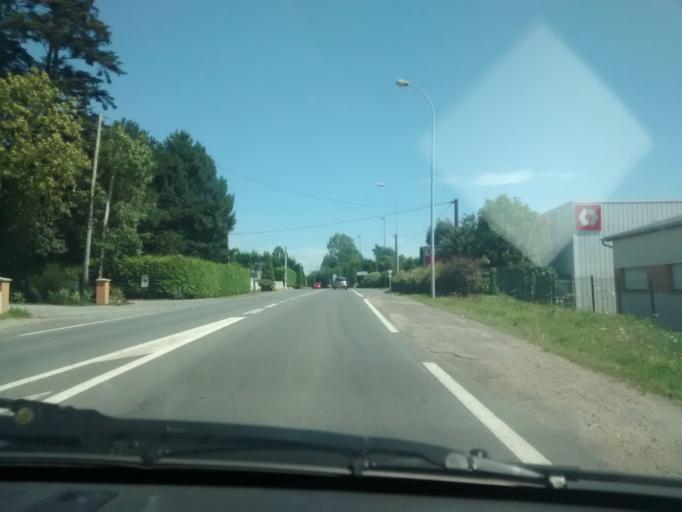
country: FR
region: Brittany
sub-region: Departement des Cotes-d'Armor
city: Ploubezre
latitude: 48.7245
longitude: -3.4368
